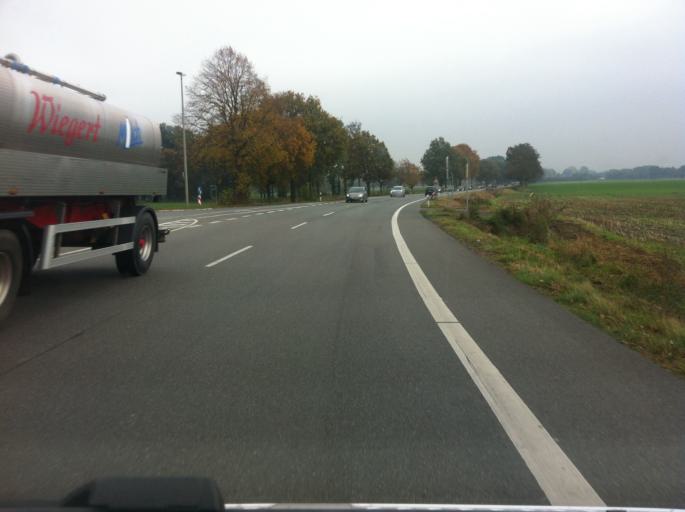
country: DE
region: North Rhine-Westphalia
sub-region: Regierungsbezirk Munster
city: Sudlohn
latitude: 51.9339
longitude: 6.8234
